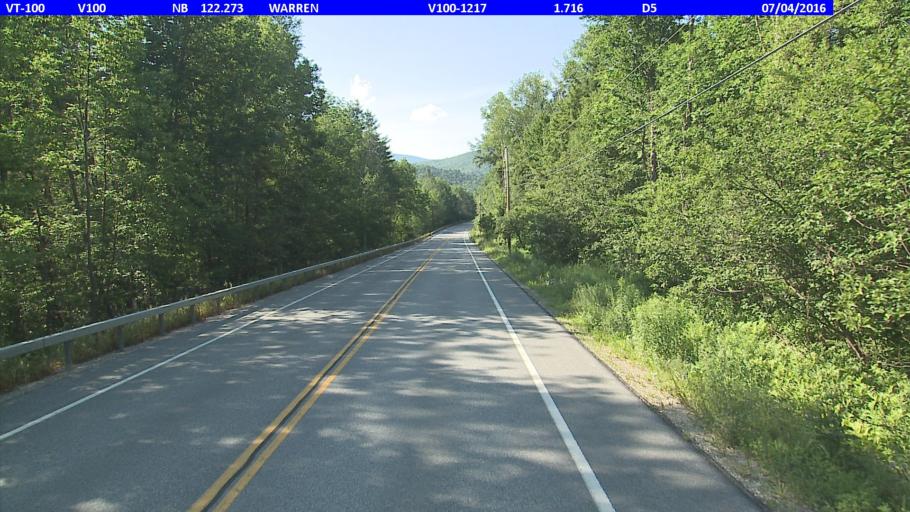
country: US
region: Vermont
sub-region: Washington County
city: Northfield
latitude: 44.0840
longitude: -72.8601
